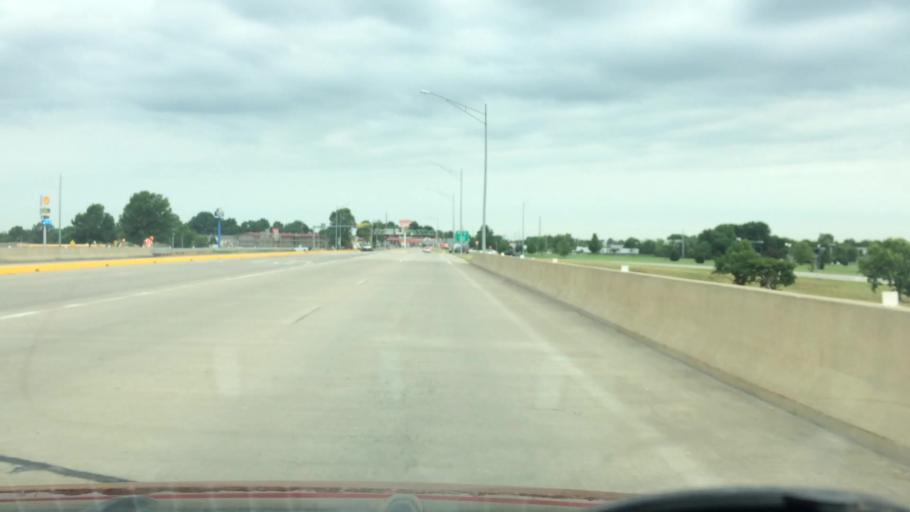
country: US
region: Missouri
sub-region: Greene County
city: Springfield
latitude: 37.2501
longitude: -93.2623
